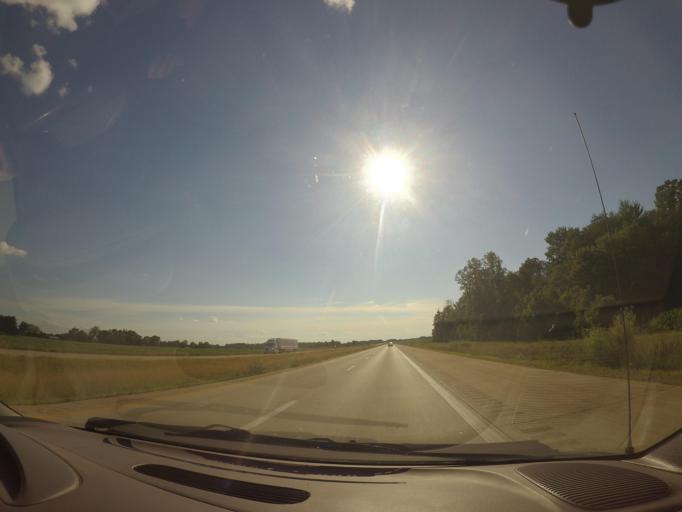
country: US
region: Ohio
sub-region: Lucas County
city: Whitehouse
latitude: 41.4561
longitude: -83.8094
